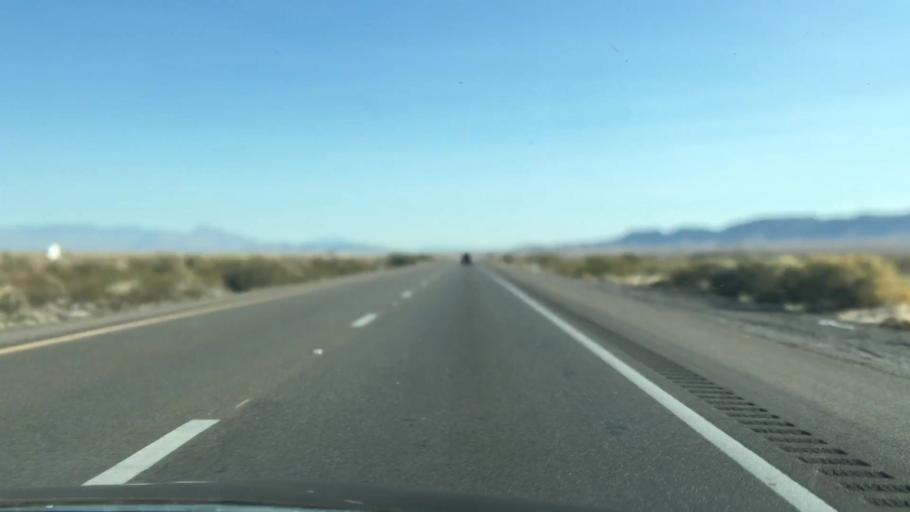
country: US
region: Nevada
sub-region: Clark County
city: Moapa Town
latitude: 36.5434
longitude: -114.7085
